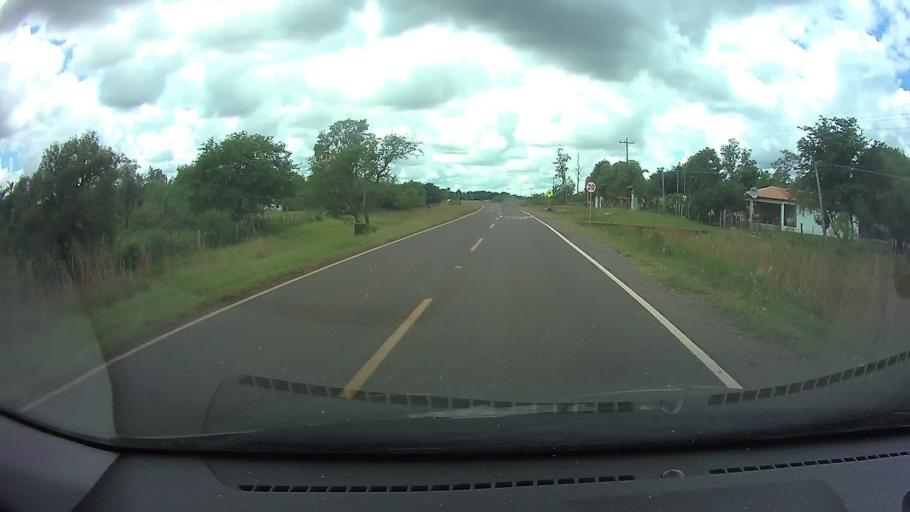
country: PY
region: Paraguari
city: Ybycui
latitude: -25.9098
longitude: -56.9867
